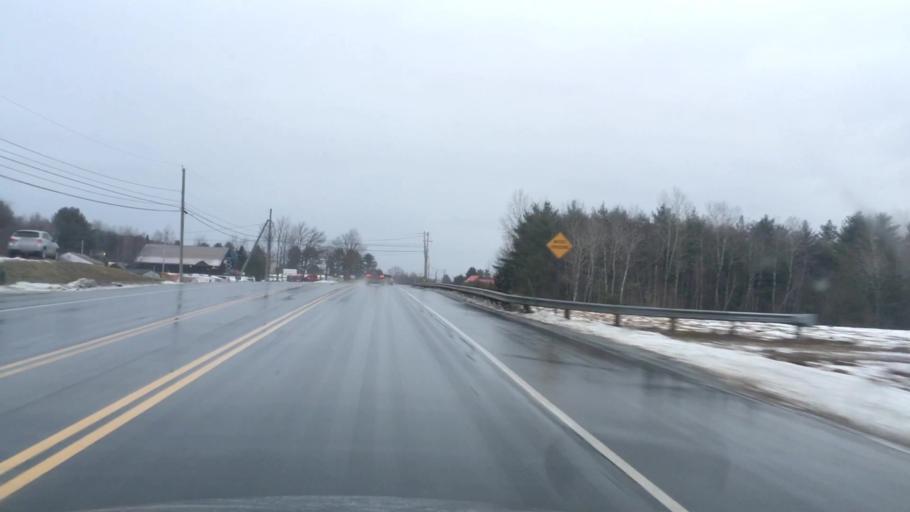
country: US
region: New Hampshire
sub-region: Sullivan County
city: Unity
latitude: 43.3676
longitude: -72.2610
